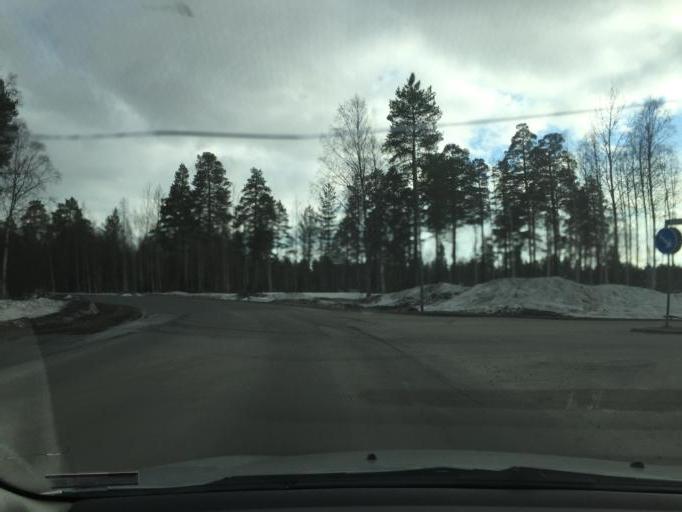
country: SE
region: Norrbotten
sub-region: Lulea Kommun
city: Lulea
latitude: 65.5919
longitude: 22.2253
